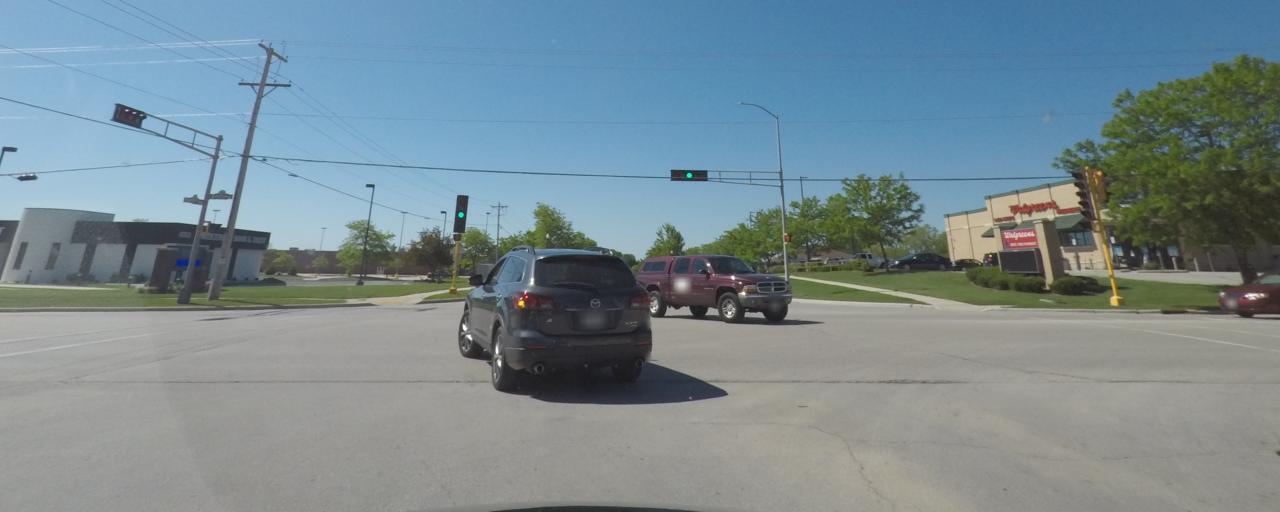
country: US
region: Wisconsin
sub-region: Sheboygan County
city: Plymouth
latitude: 43.7472
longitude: -87.9513
